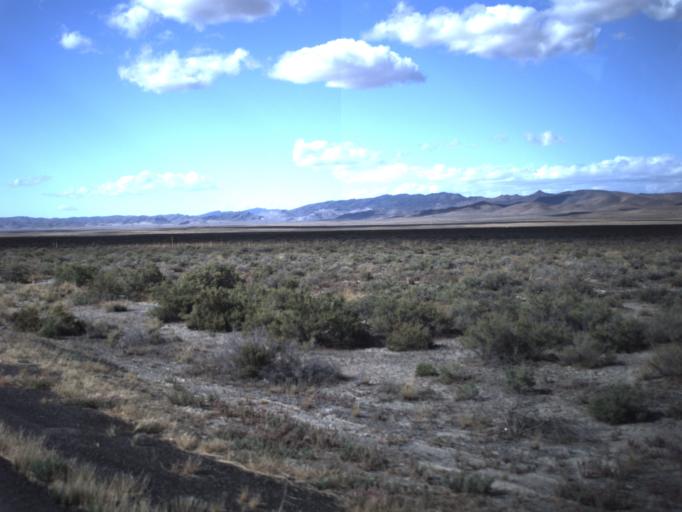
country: US
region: Utah
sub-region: Millard County
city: Delta
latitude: 39.0578
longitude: -112.7645
